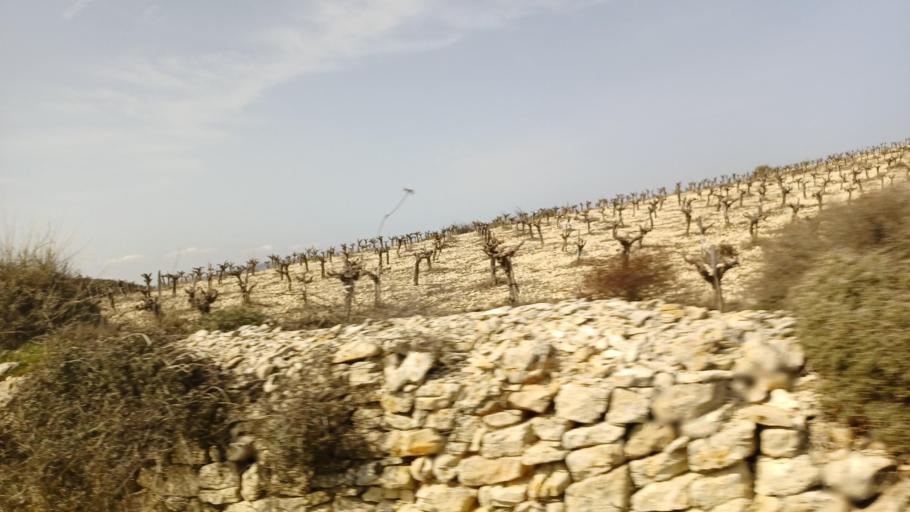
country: CY
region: Limassol
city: Pachna
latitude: 34.8029
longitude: 32.7490
